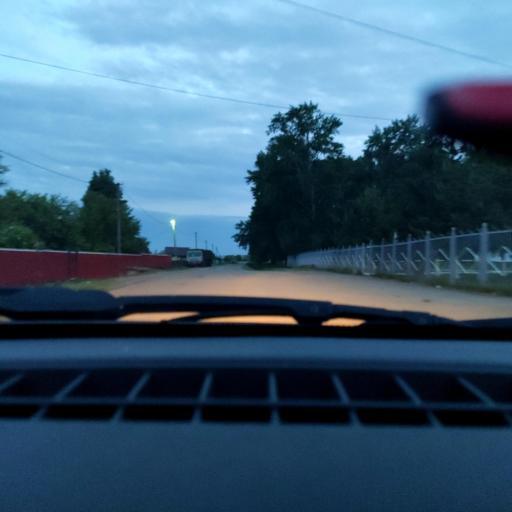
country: RU
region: Bashkortostan
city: Tolbazy
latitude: 54.2969
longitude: 55.8099
